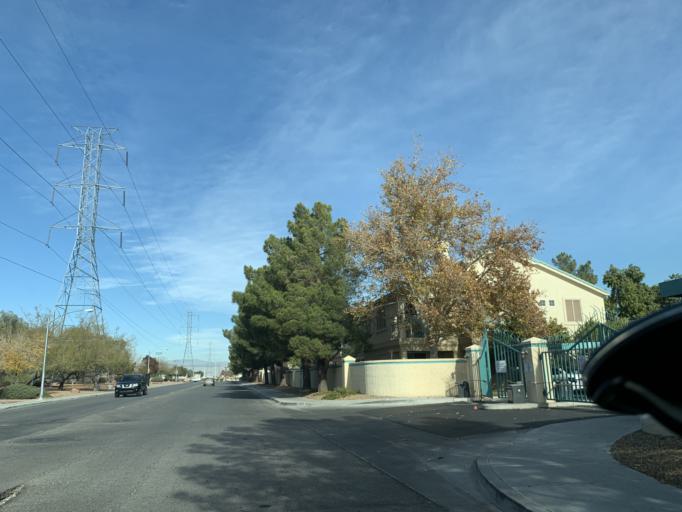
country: US
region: Nevada
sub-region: Clark County
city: Spring Valley
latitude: 36.0987
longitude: -115.2122
